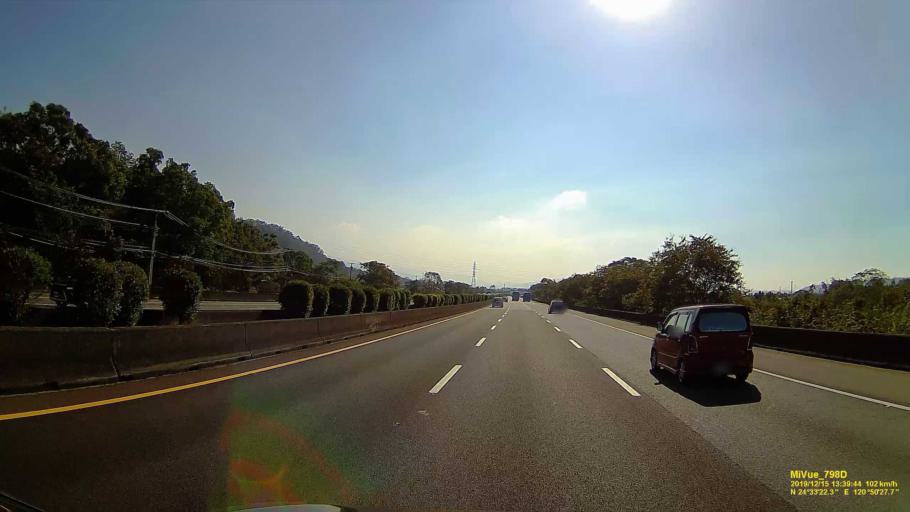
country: TW
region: Taiwan
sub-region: Miaoli
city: Miaoli
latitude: 24.5557
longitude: 120.8412
